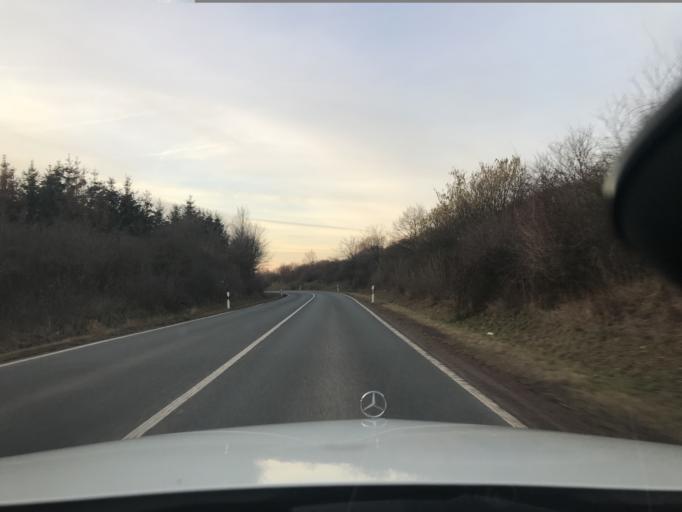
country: DE
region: Thuringia
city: Ernstroda
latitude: 50.8861
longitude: 10.6541
